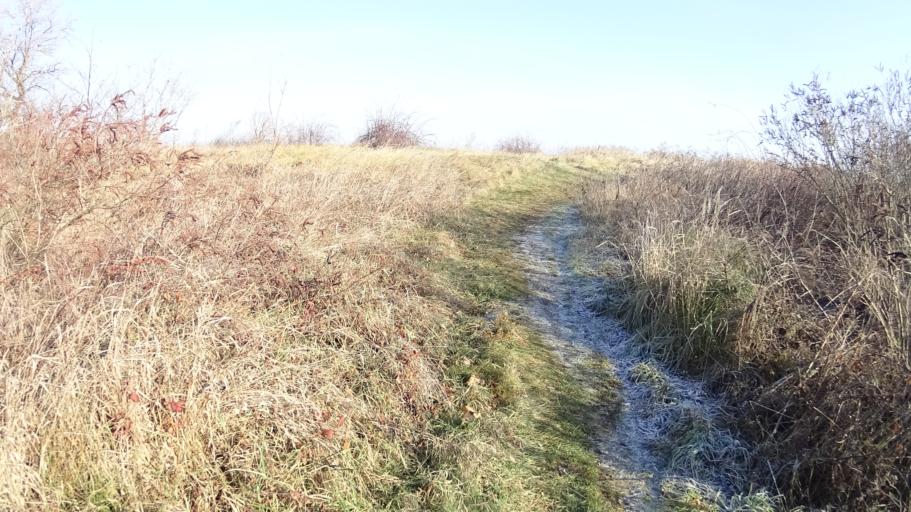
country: HU
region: Borsod-Abauj-Zemplen
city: Nyekladhaza
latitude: 47.9922
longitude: 20.8677
